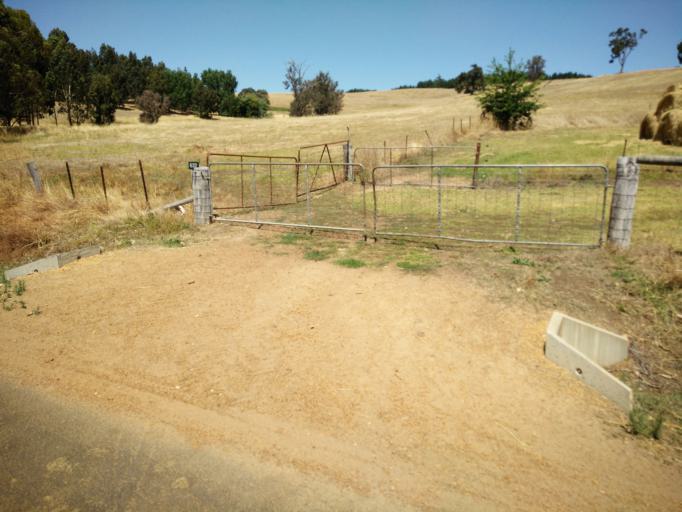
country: AU
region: Western Australia
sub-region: Bridgetown-Greenbushes
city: Bridgetown
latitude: -33.9350
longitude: 116.0277
